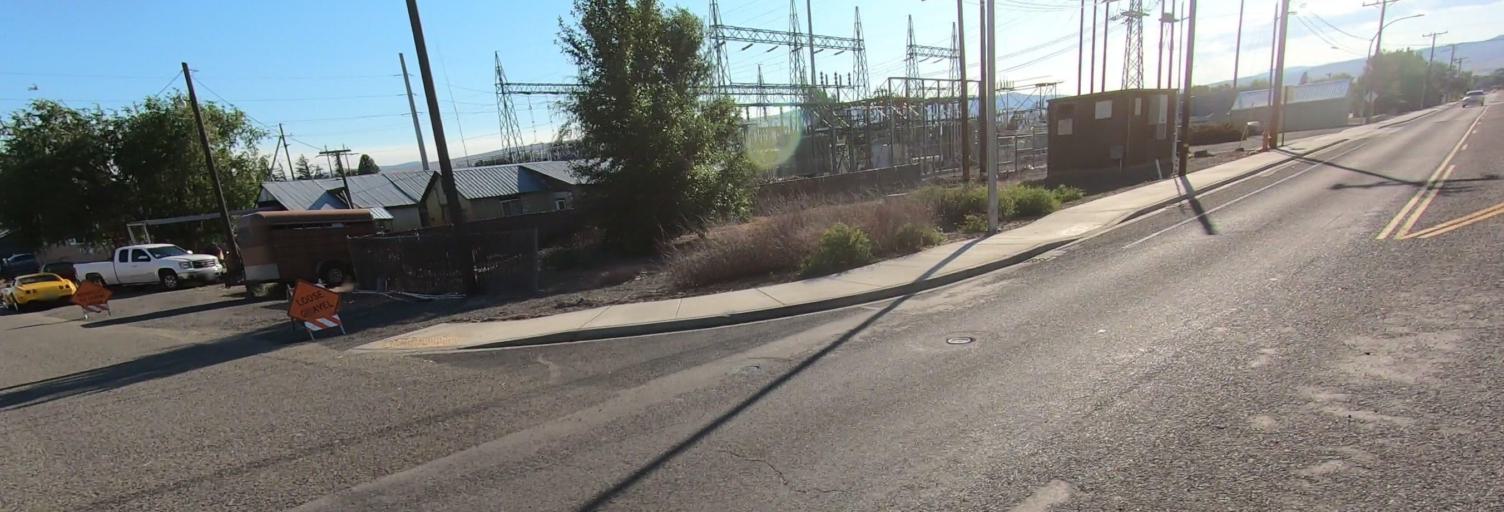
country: US
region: Washington
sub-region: Kittitas County
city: Ellensburg
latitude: 46.9994
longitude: -120.5628
